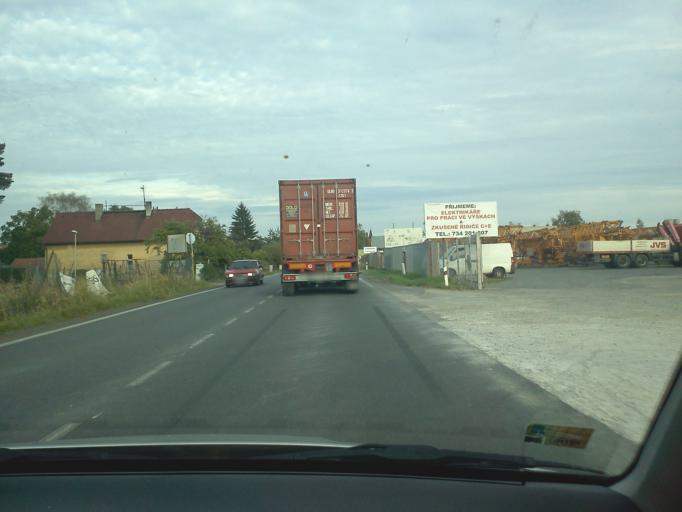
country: CZ
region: Central Bohemia
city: Mukarov
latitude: 49.9900
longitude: 14.7289
